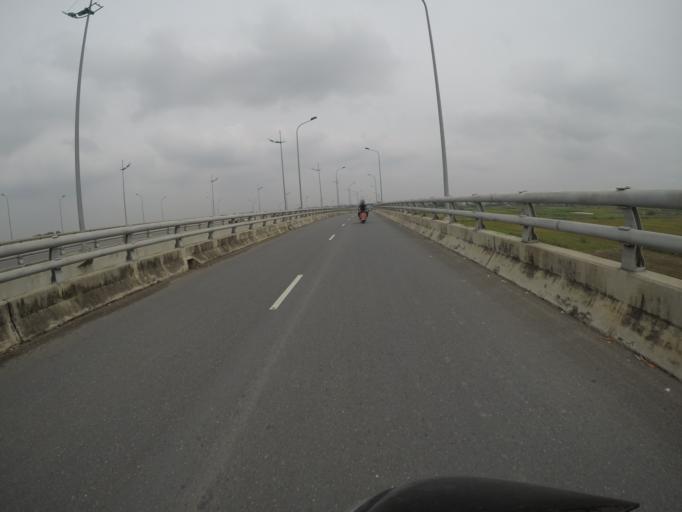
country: VN
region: Ha Noi
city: Dong Anh
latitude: 21.1649
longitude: 105.8200
